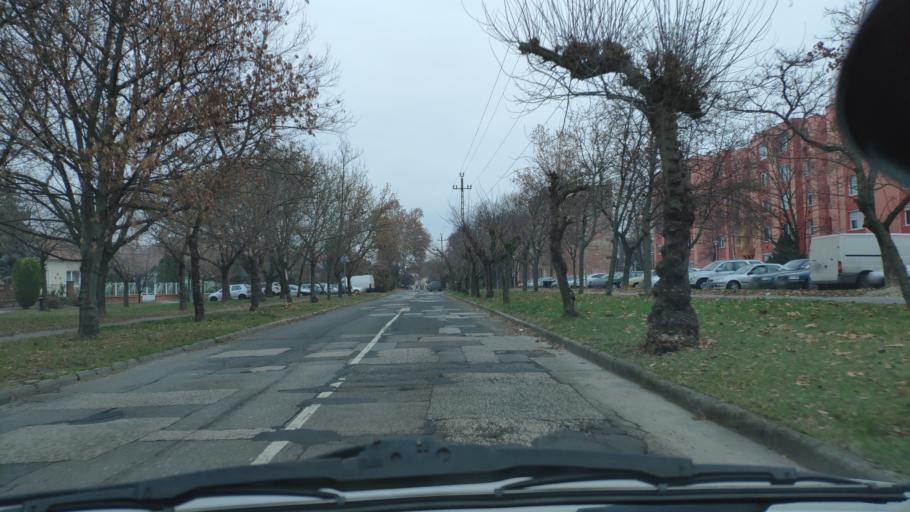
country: HU
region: Budapest
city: Budapest XXI. keruelet
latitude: 47.4063
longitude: 19.0778
